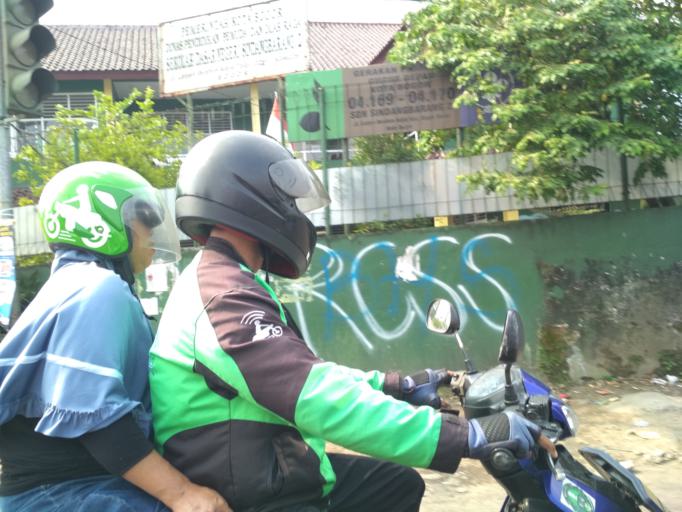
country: ID
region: West Java
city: Bogor
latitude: -6.5804
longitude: 106.7633
